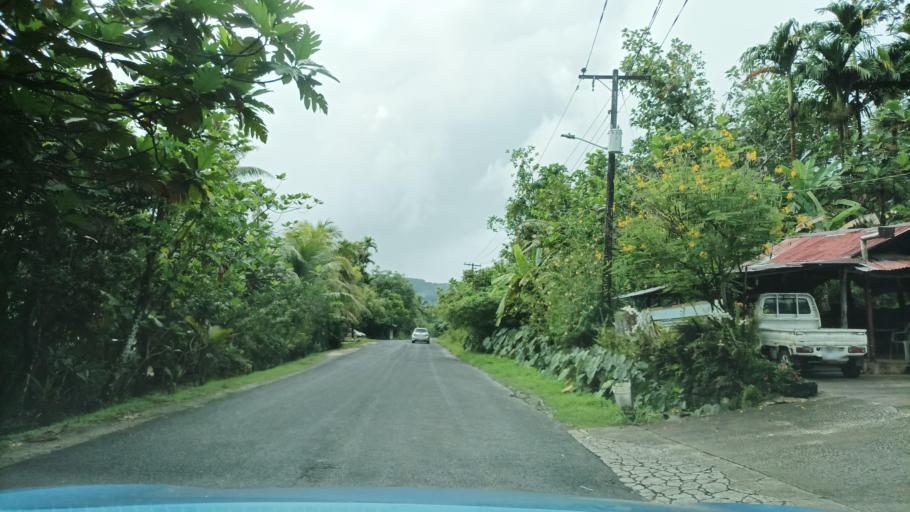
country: FM
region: Pohnpei
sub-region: Kolonia Municipality
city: Kolonia
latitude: 6.9323
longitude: 158.2777
